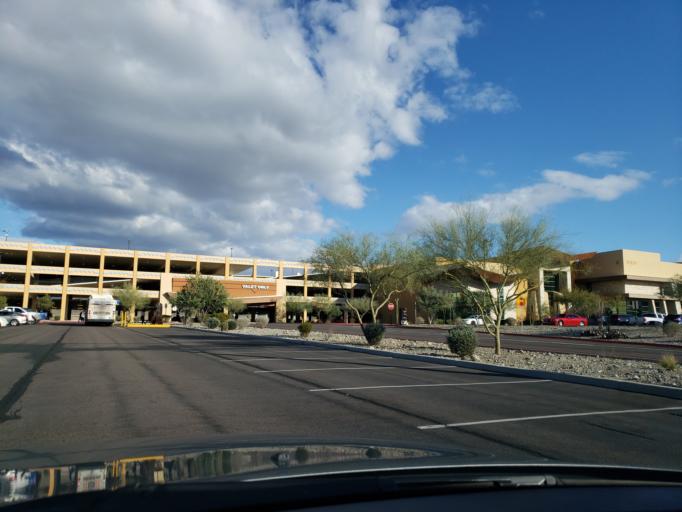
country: US
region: Arizona
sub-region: Maricopa County
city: Laveen
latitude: 33.3108
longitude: -112.1588
